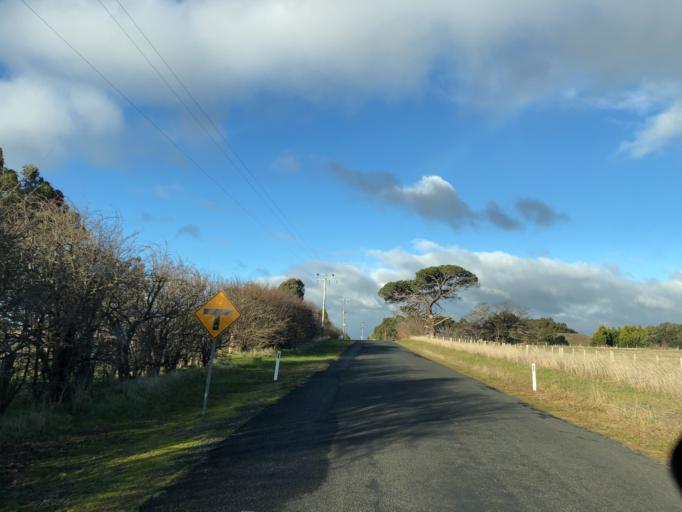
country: AU
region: Victoria
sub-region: Mount Alexander
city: Castlemaine
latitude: -37.2149
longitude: 144.3463
